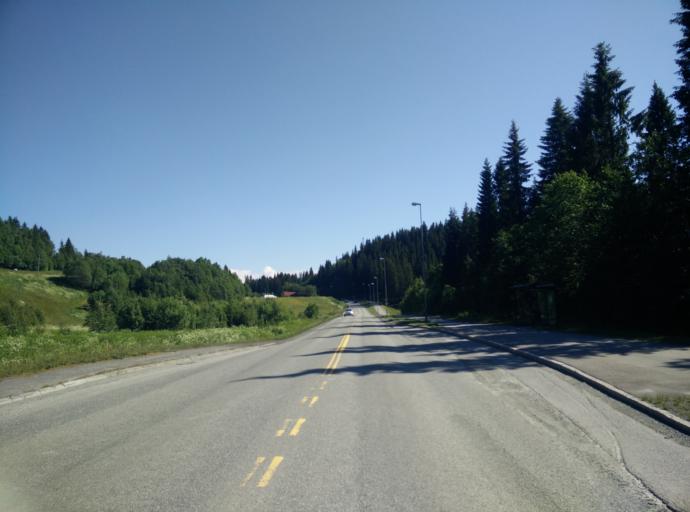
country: NO
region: Sor-Trondelag
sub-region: Trondheim
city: Trondheim
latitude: 63.3791
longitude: 10.3167
